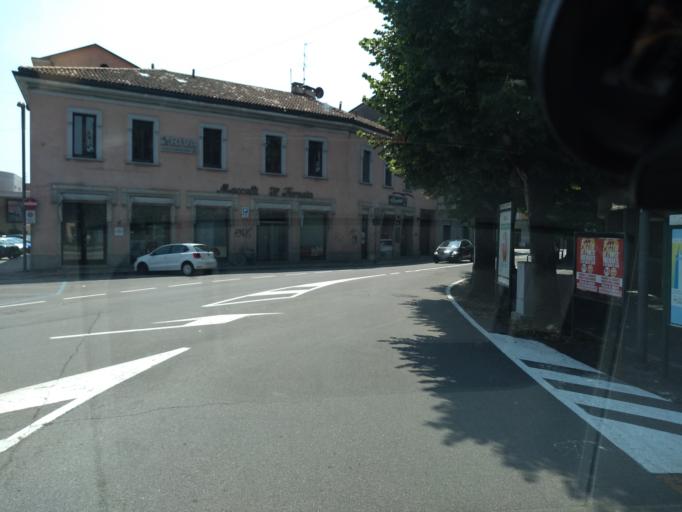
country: IT
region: Lombardy
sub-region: Provincia di Bergamo
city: Treviglio
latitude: 45.5203
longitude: 9.5953
